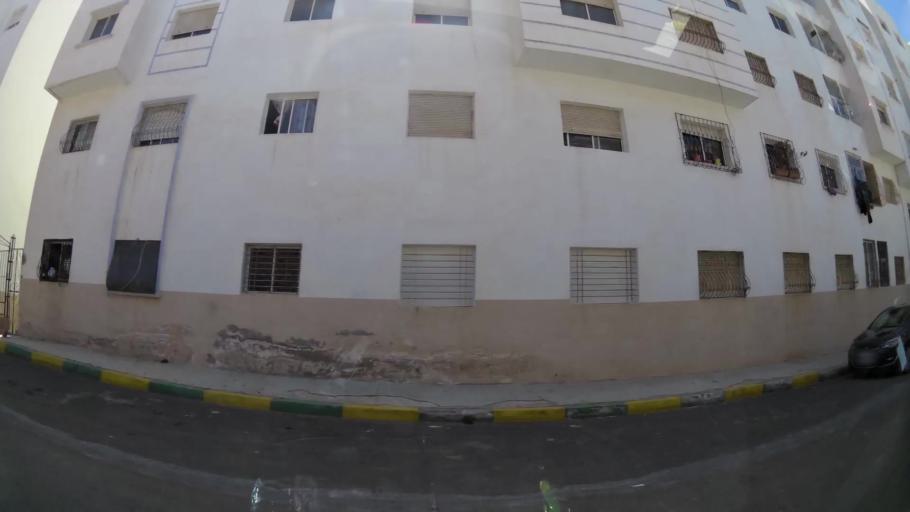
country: MA
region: Oued ed Dahab-Lagouira
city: Dakhla
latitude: 30.4408
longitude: -9.5642
